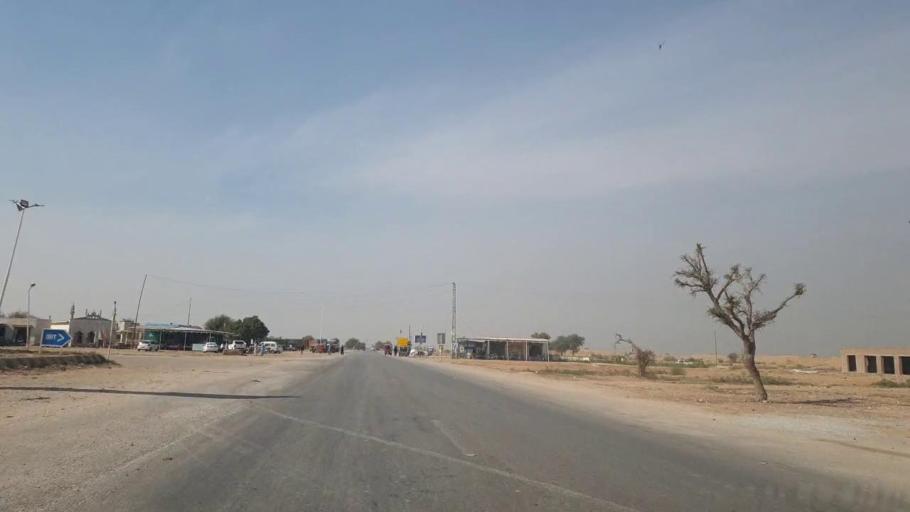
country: PK
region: Sindh
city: Sann
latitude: 26.0278
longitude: 68.1256
